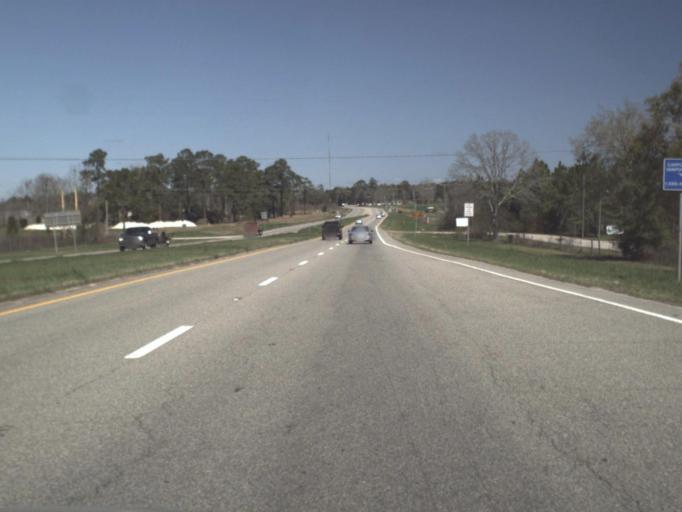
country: US
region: Florida
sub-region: Gadsden County
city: Quincy
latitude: 30.5405
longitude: -84.5944
